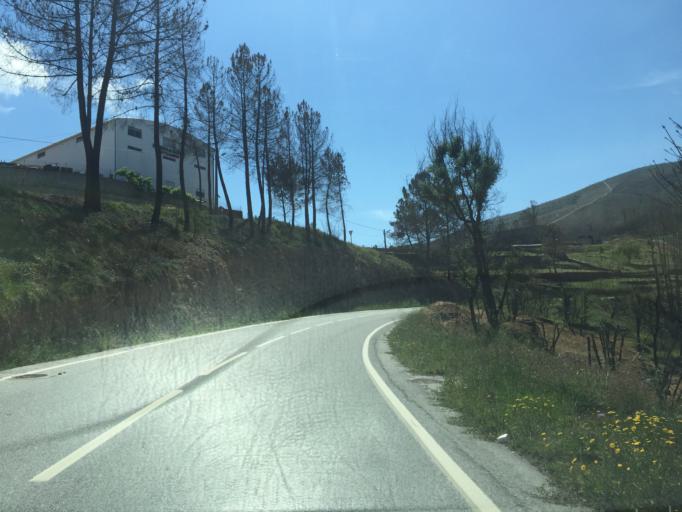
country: PT
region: Coimbra
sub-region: Pampilhosa da Serra
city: Pampilhosa da Serra
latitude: 40.0432
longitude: -7.9555
